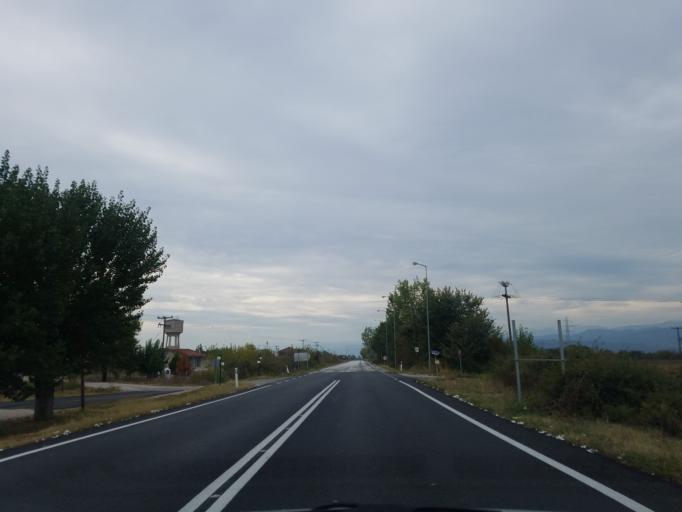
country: GR
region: Thessaly
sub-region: Nomos Kardhitsas
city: Agnantero
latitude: 39.4949
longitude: 21.8385
